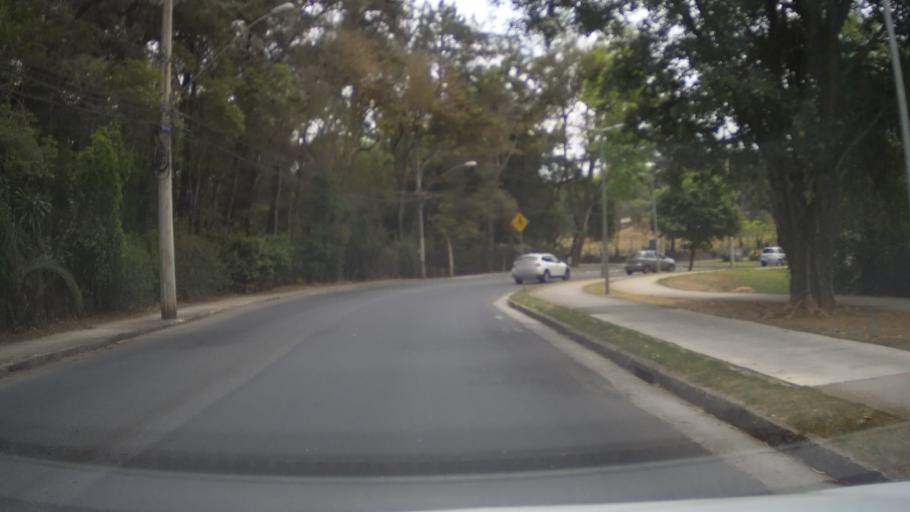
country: BR
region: Minas Gerais
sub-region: Contagem
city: Contagem
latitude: -19.8517
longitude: -44.0055
